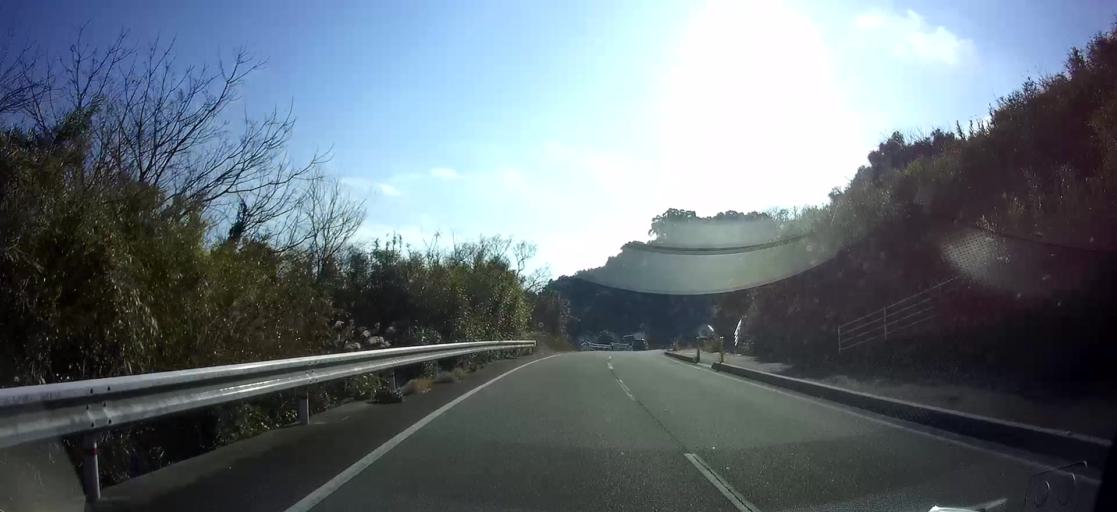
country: JP
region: Kumamoto
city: Minamata
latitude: 32.3992
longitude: 130.3988
